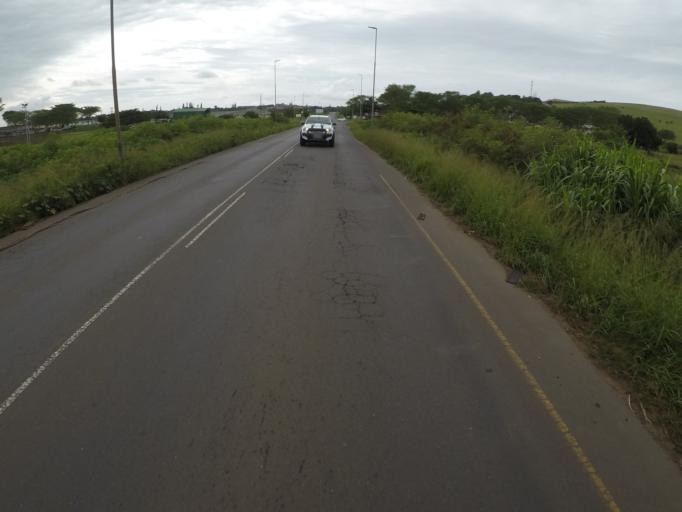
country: ZA
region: KwaZulu-Natal
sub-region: uThungulu District Municipality
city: Empangeni
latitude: -28.7340
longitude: 31.8762
